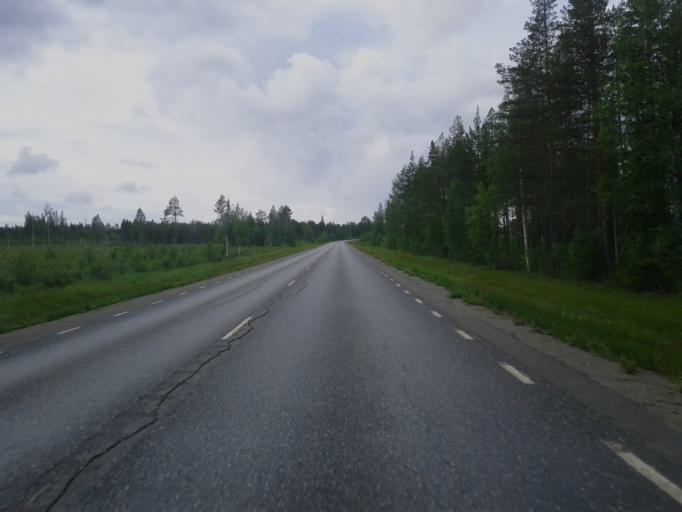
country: SE
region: Vaesterbotten
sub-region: Norsjo Kommun
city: Norsjoe
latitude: 64.9871
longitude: 19.4010
